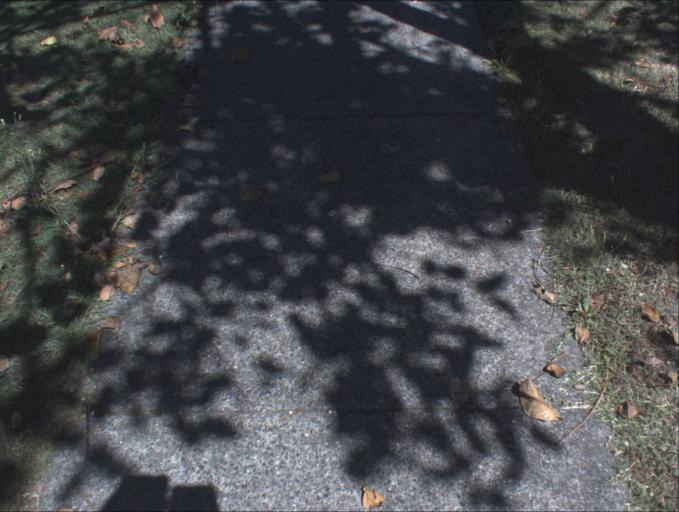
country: AU
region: Queensland
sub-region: Logan
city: Windaroo
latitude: -27.7240
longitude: 153.2050
